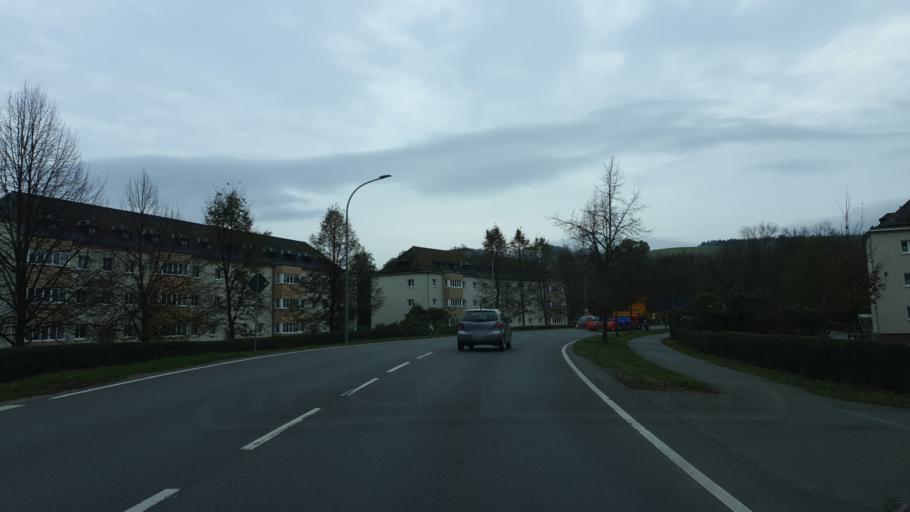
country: DE
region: Saxony
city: Schwarzenberg
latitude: 50.5451
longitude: 12.7926
